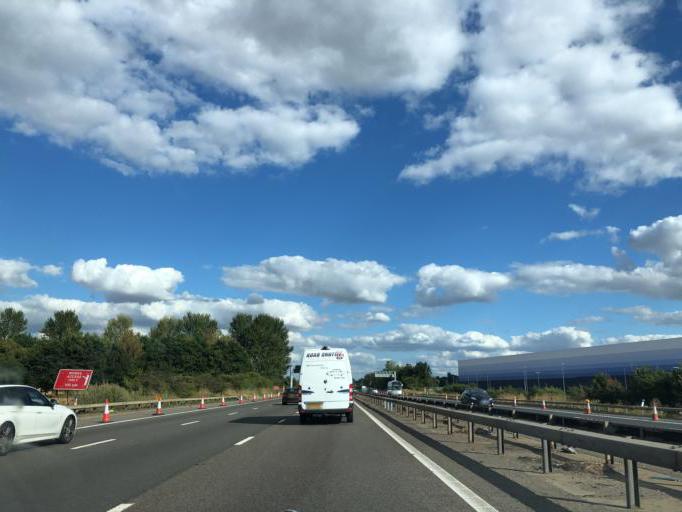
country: GB
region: England
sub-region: Milton Keynes
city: Wavendon
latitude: 52.0425
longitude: -0.6554
